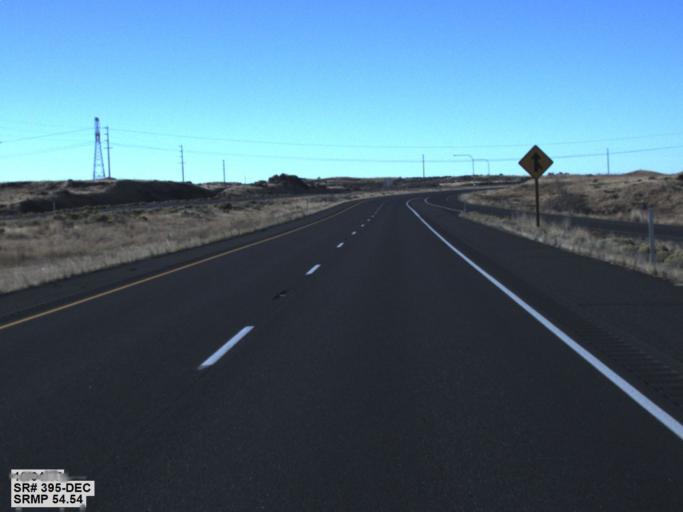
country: US
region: Washington
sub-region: Franklin County
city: Connell
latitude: 46.6472
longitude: -118.8564
